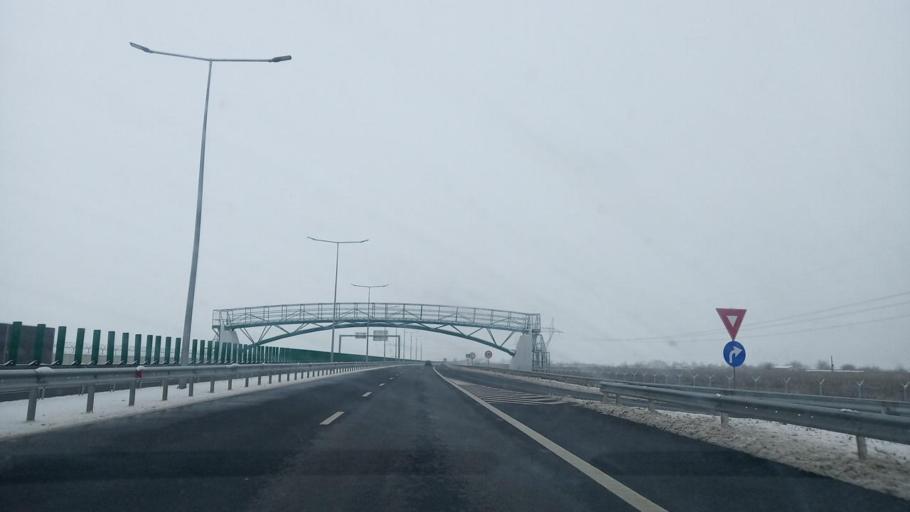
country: RO
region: Bacau
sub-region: Comuna Letea Veche
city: Holt
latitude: 46.5903
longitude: 26.9616
